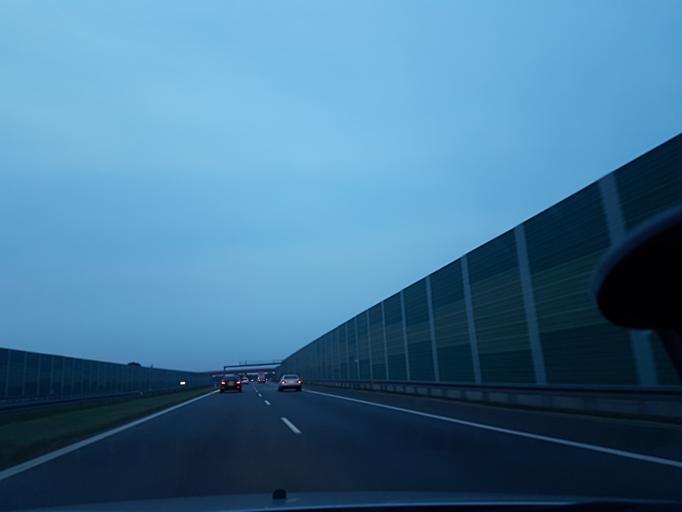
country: PL
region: Lodz Voivodeship
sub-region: Powiat kutnowski
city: Krzyzanow
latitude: 52.2157
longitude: 19.4758
